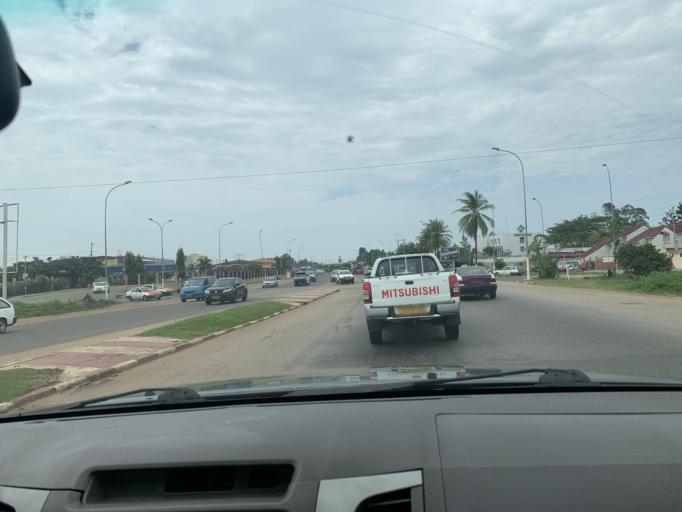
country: GA
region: Estuaire
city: Libreville
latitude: 0.3385
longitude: 9.4787
